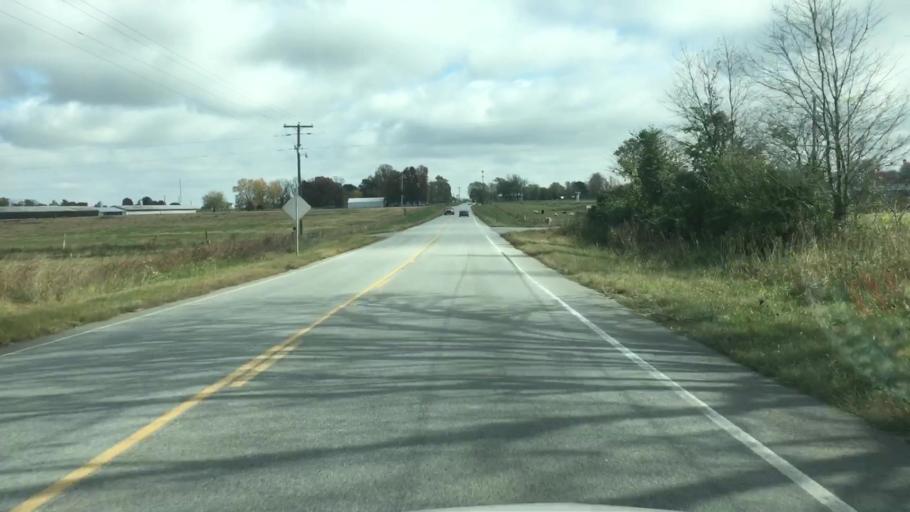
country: US
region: Arkansas
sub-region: Benton County
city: Gentry
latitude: 36.2618
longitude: -94.3647
